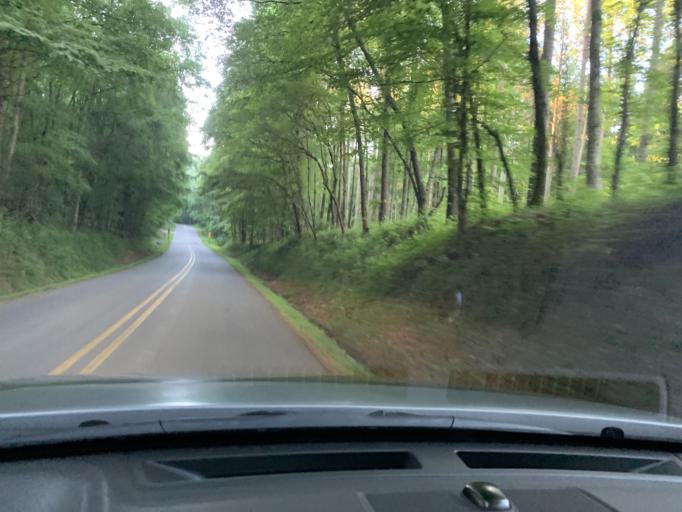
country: US
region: Georgia
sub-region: Bartow County
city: Rydal
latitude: 34.2353
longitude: -84.6650
